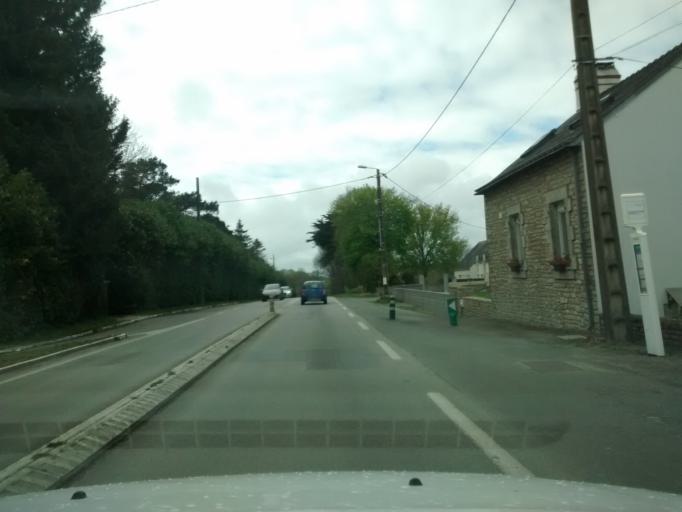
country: FR
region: Brittany
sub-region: Departement du Morbihan
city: Gestel
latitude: 47.7808
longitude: -3.4414
